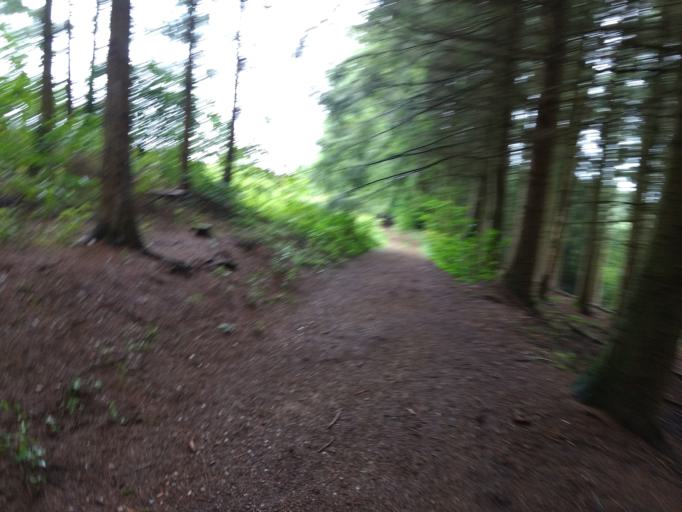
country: BE
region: Wallonia
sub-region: Province du Luxembourg
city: Houffalize
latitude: 50.1601
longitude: 5.7174
